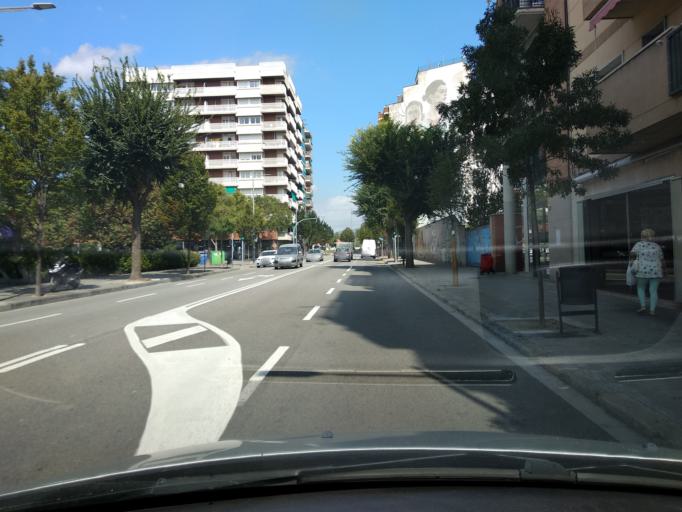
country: ES
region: Catalonia
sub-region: Provincia de Barcelona
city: Granollers
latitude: 41.6093
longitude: 2.2834
